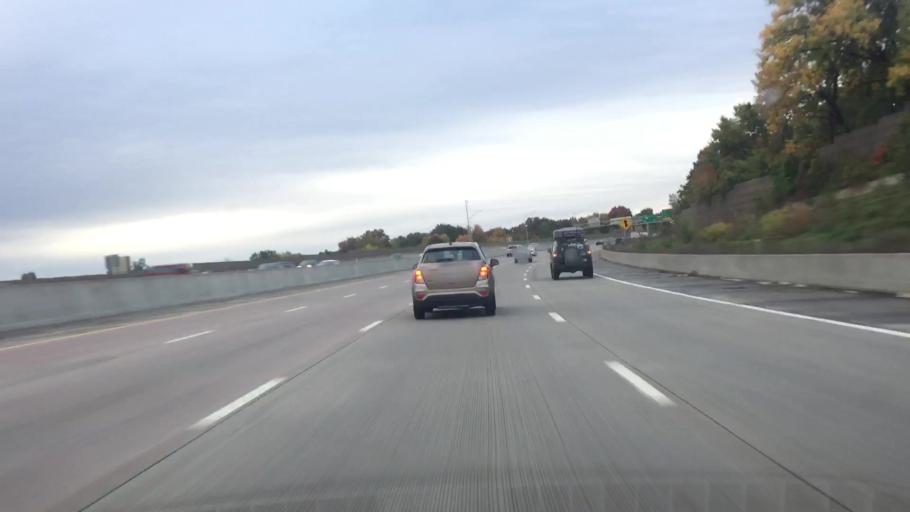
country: US
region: Kansas
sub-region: Johnson County
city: Lenexa
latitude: 38.9562
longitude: -94.7093
